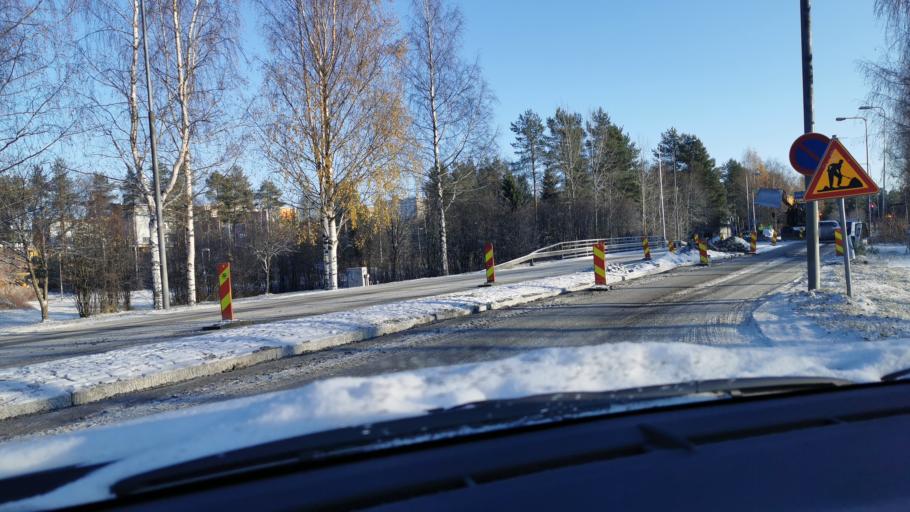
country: FI
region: Northern Ostrobothnia
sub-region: Oulu
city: Oulu
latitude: 65.0555
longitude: 25.4695
